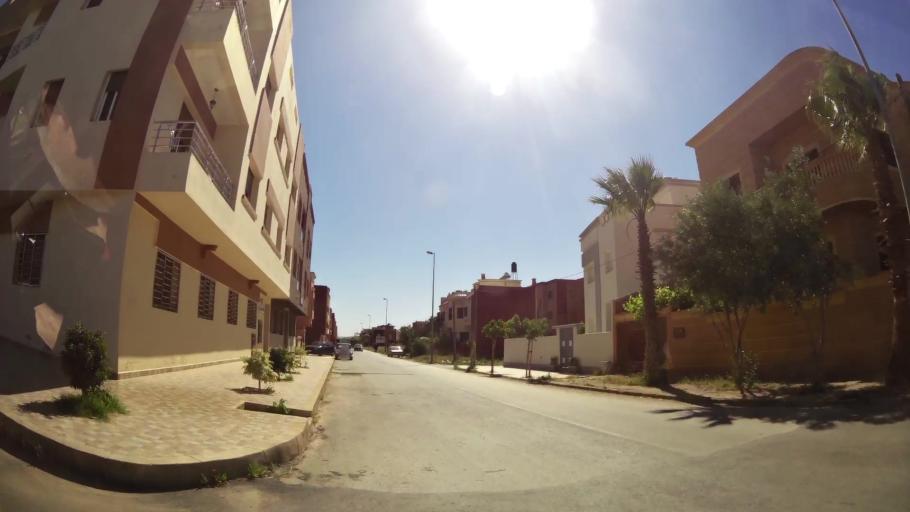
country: MA
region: Oriental
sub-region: Berkane-Taourirt
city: Berkane
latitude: 34.9452
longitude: -2.3291
